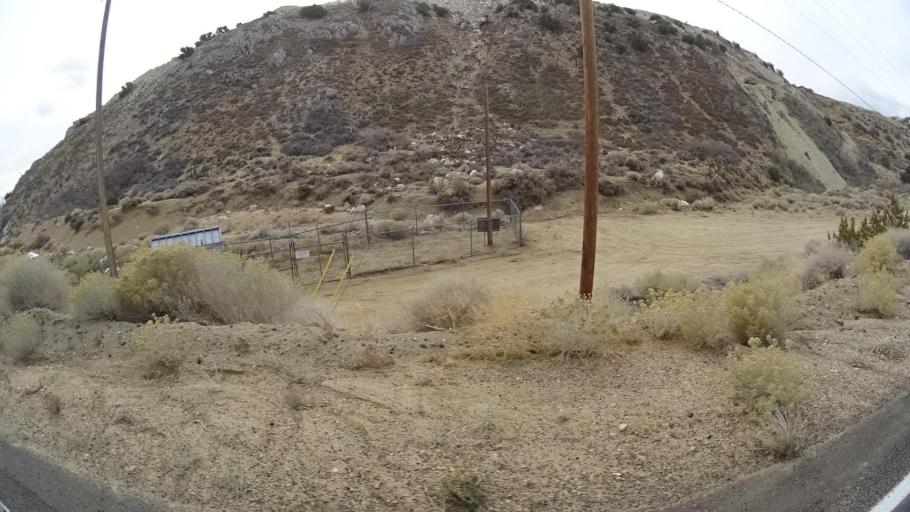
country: US
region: California
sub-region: Kern County
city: Tehachapi
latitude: 35.0525
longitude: -118.3336
